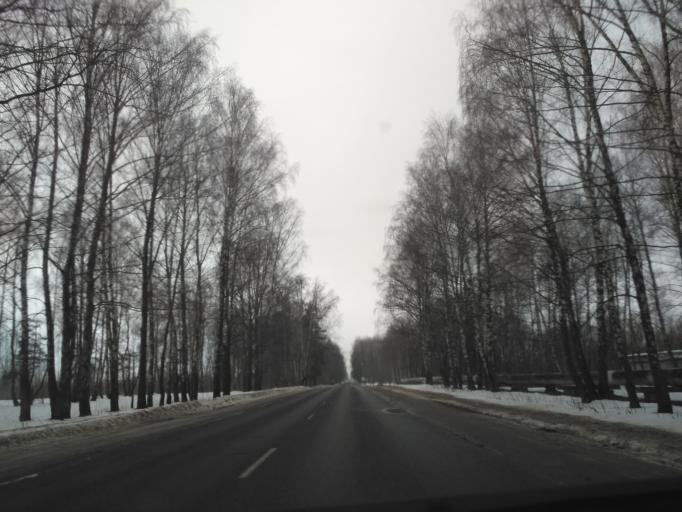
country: BY
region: Minsk
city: Horad Zhodzina
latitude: 54.0875
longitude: 28.3226
